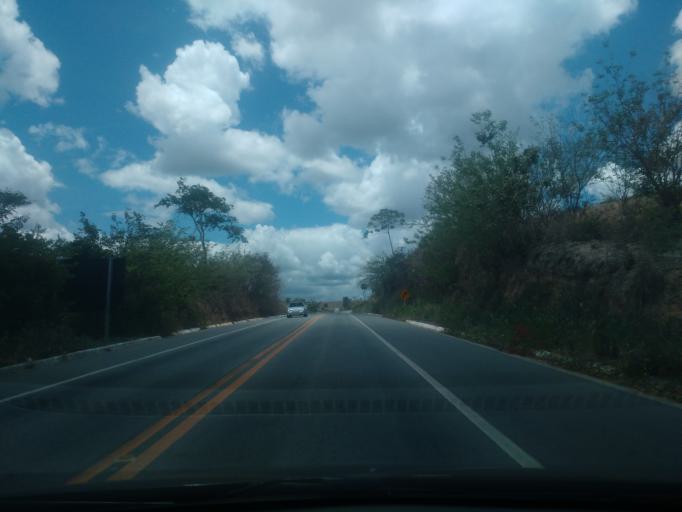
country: BR
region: Alagoas
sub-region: Murici
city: Murici
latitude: -9.2457
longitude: -36.0053
